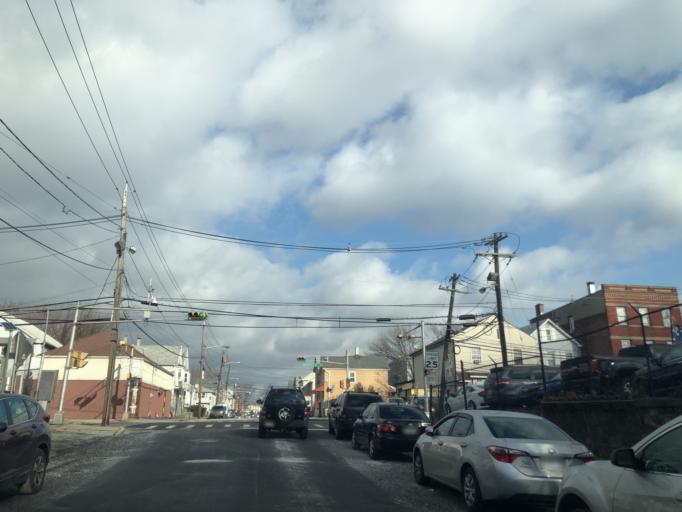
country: US
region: New Jersey
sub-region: Union County
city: Elizabeth
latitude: 40.6672
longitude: -74.2065
